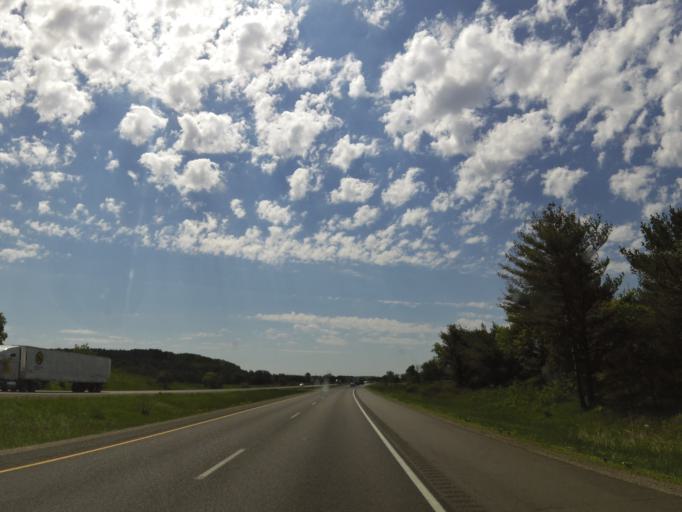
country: US
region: Wisconsin
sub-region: Eau Claire County
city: Fall Creek
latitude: 44.7178
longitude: -91.3501
